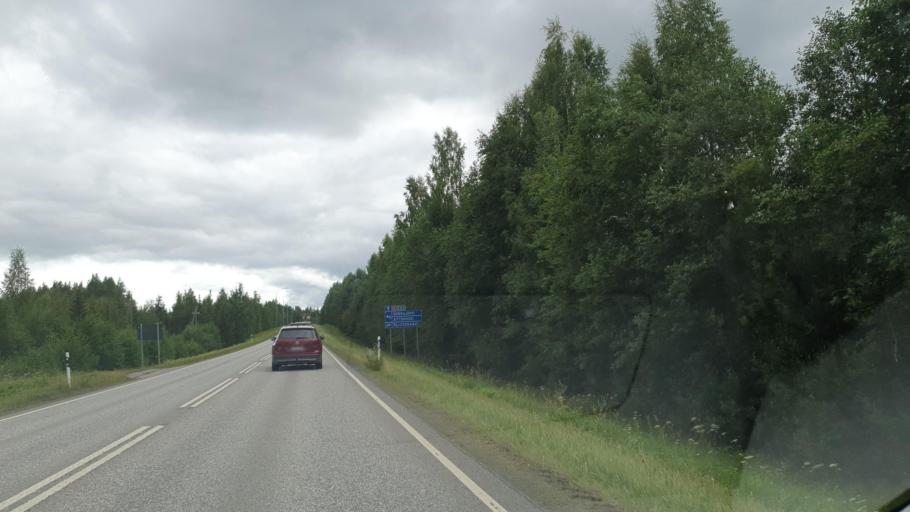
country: FI
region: Northern Savo
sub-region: Ylae-Savo
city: Sonkajaervi
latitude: 63.7022
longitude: 27.3568
